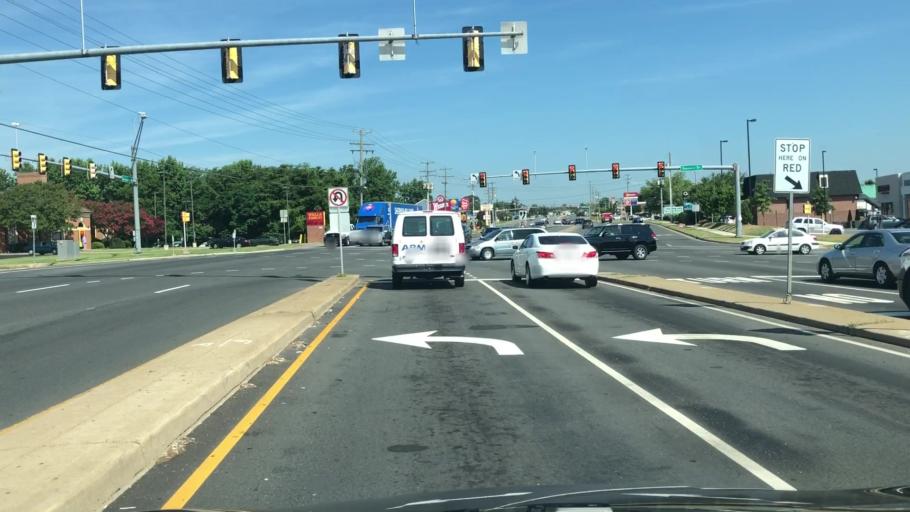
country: US
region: Virginia
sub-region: Stafford County
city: Aquia Harbour
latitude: 38.4683
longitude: -77.4117
